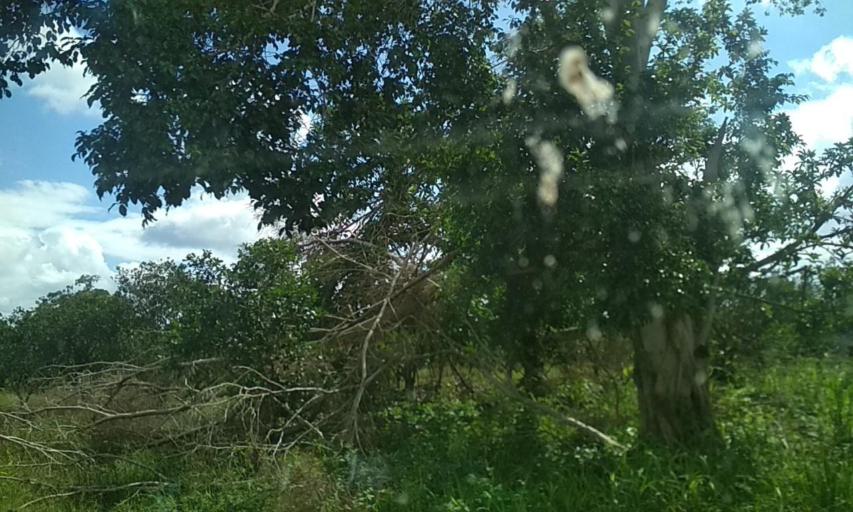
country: MX
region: Puebla
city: San Jose Acateno
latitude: 20.2787
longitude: -97.1316
